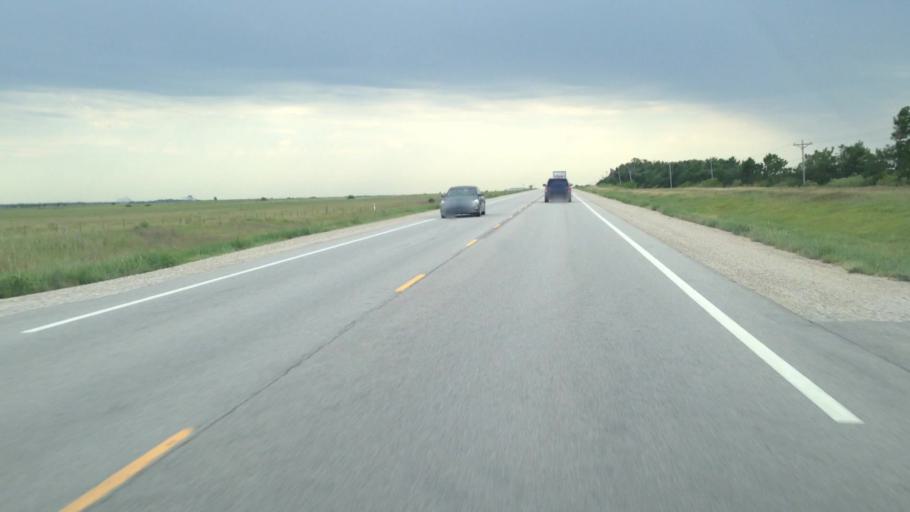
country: US
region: Kansas
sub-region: Coffey County
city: Burlington
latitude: 38.3179
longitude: -95.7290
